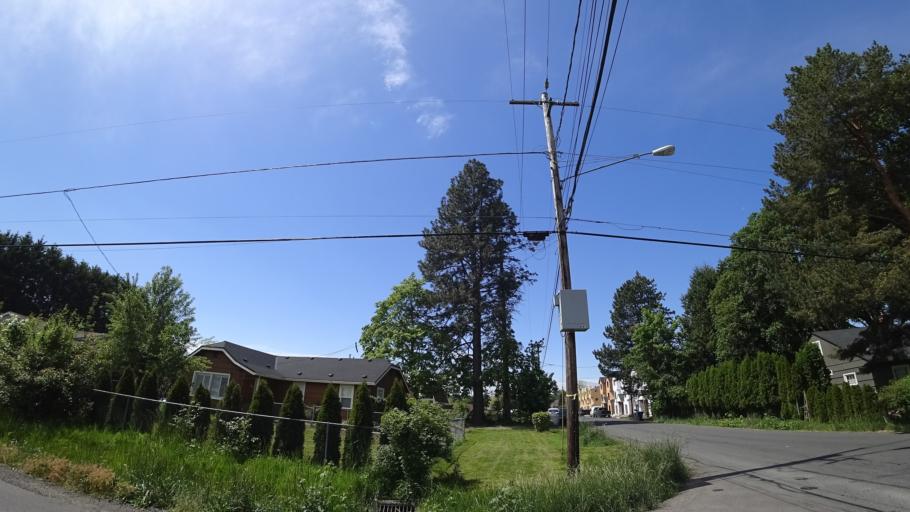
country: US
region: Oregon
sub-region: Washington County
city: Aloha
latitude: 45.4899
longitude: -122.8468
